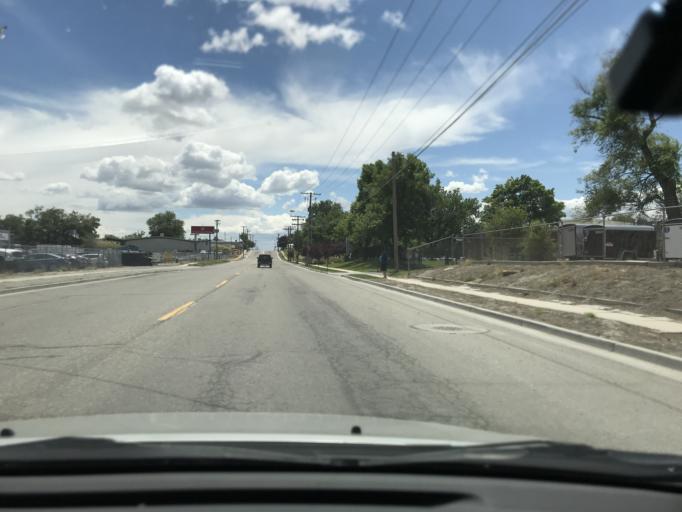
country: US
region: Utah
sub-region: Salt Lake County
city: Centerfield
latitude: 40.6802
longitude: -111.8998
